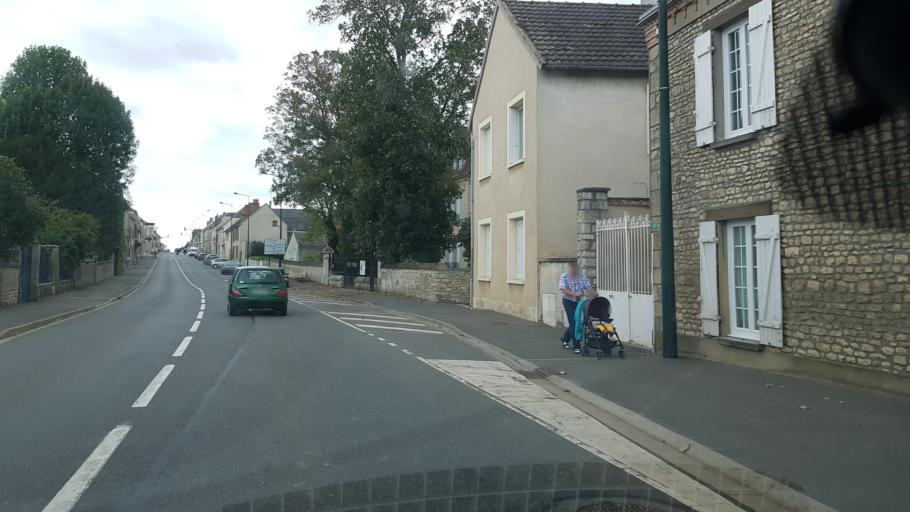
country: FR
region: Centre
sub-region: Departement du Loiret
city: Sermaises
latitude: 48.2980
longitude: 2.2004
